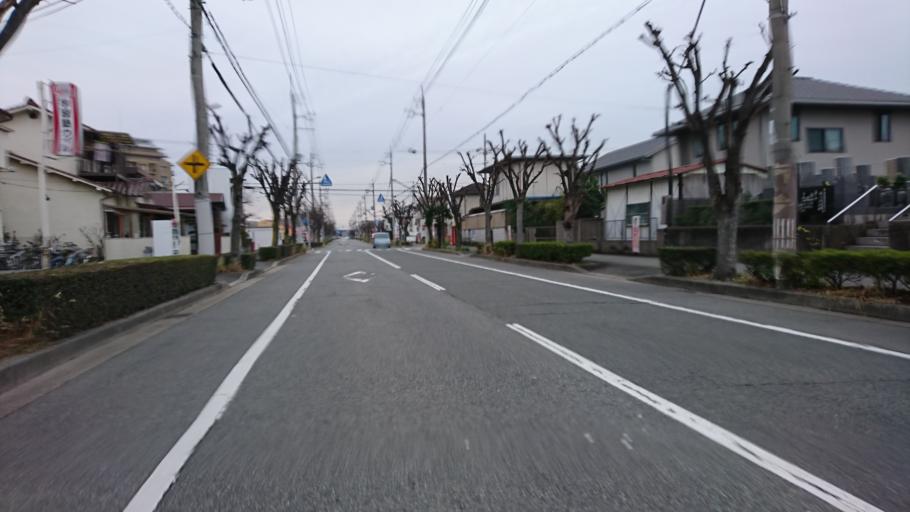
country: JP
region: Hyogo
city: Kakogawacho-honmachi
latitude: 34.7586
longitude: 134.8305
